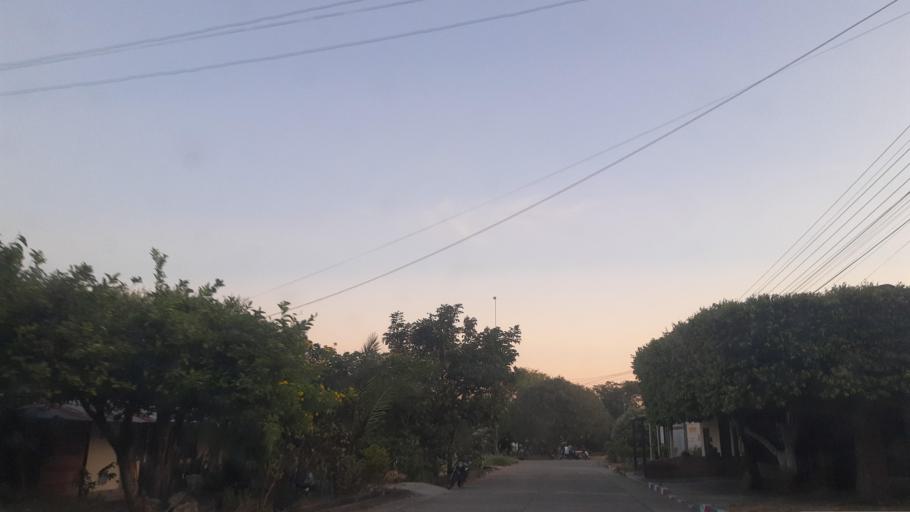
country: CO
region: Arauca
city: Tame
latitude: 6.4561
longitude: -71.7315
